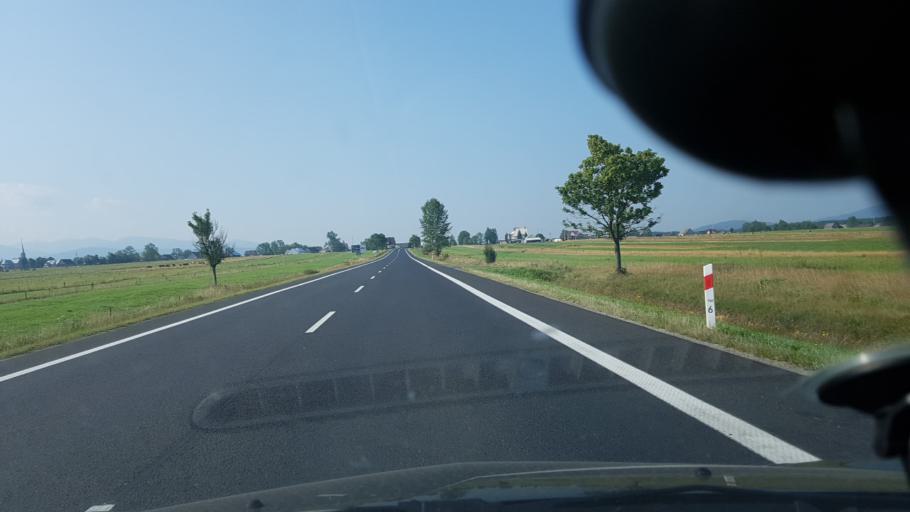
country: PL
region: Lesser Poland Voivodeship
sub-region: Powiat nowotarski
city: Chyzne
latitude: 49.4325
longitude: 19.6779
